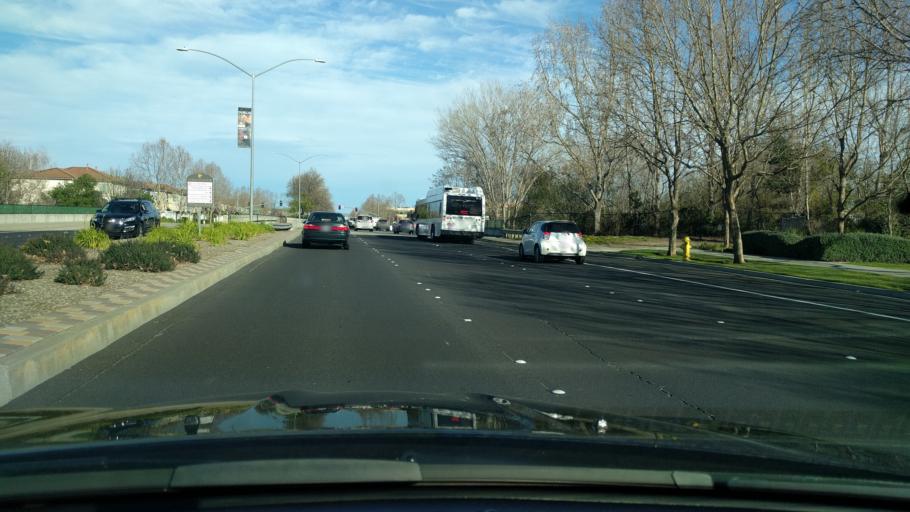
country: US
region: California
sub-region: Alameda County
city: Pleasanton
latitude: 37.7056
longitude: -121.8793
